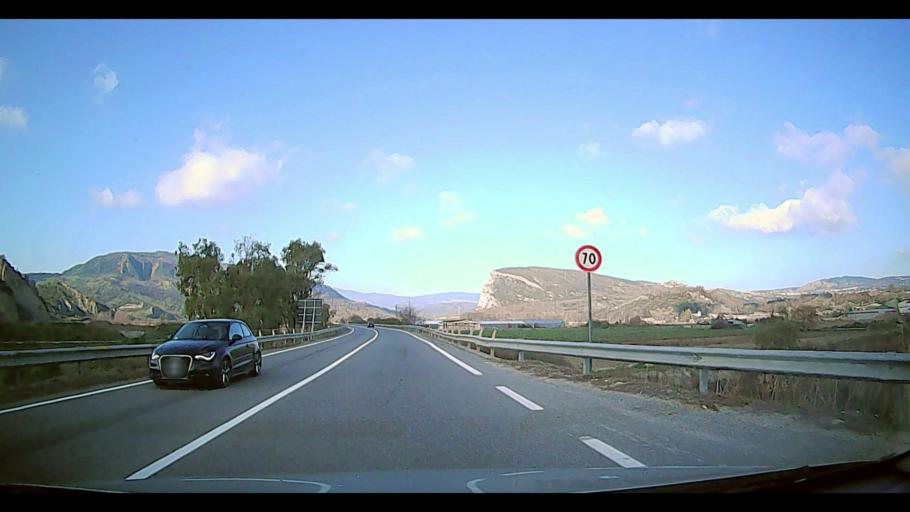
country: IT
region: Calabria
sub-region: Provincia di Crotone
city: Santa Severina
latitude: 39.1798
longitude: 16.9203
